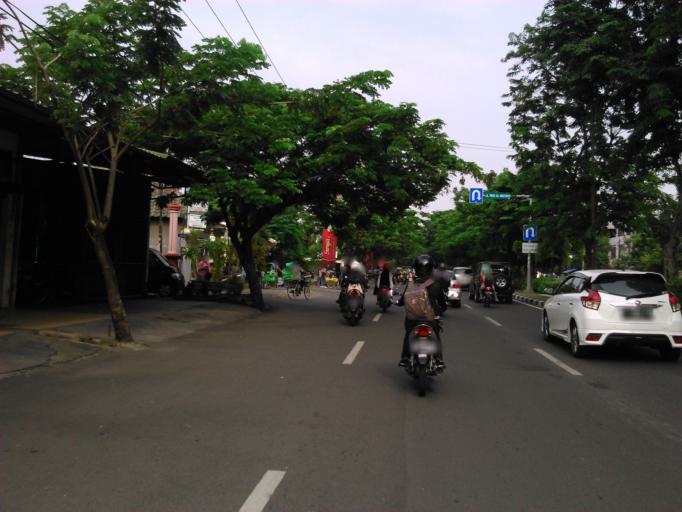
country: ID
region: East Java
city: Brongkalan
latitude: -7.2663
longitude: 112.7666
